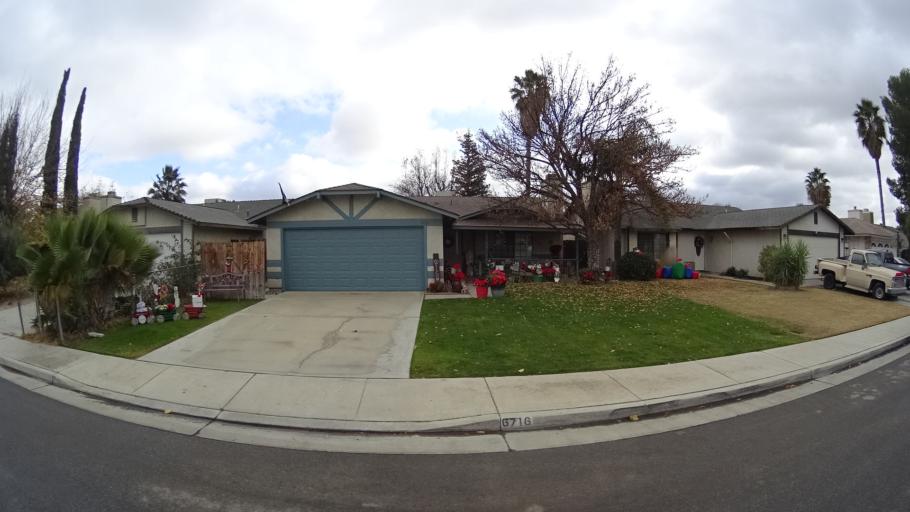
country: US
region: California
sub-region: Kern County
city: Greenfield
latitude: 35.2939
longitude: -119.0178
